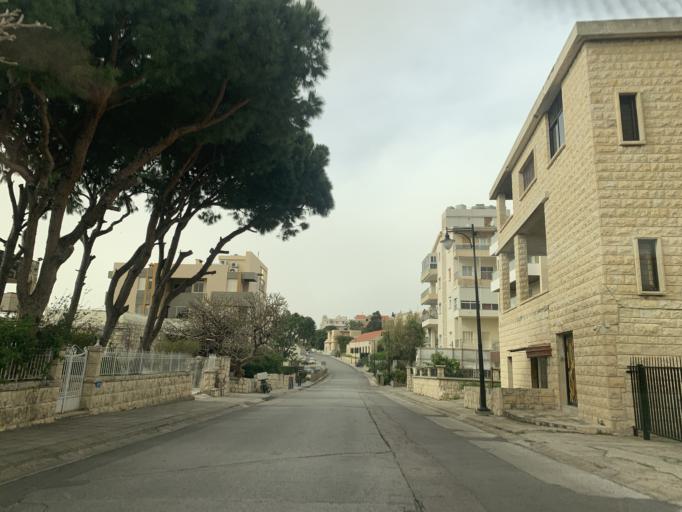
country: LB
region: Mont-Liban
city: Jbail
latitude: 34.0962
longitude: 35.6521
